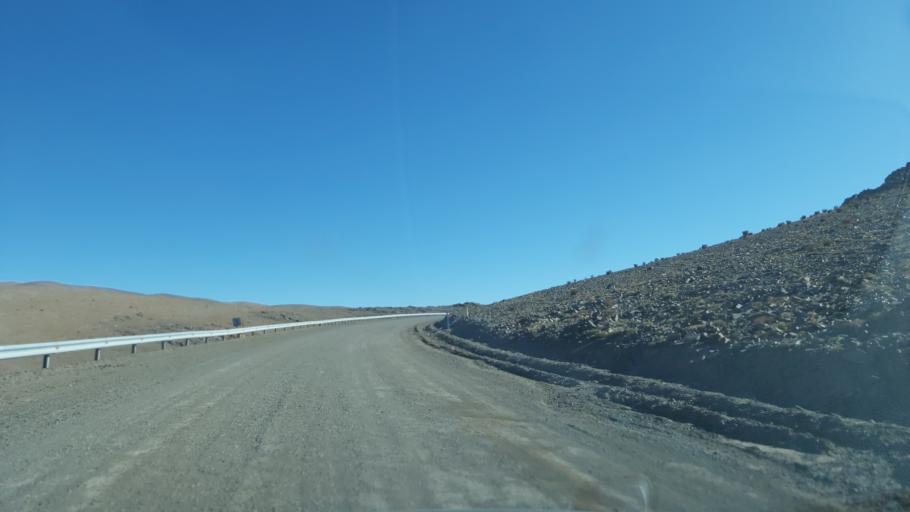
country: CL
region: Atacama
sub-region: Provincia de Chanaral
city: Diego de Almagro
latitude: -26.4296
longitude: -69.2801
